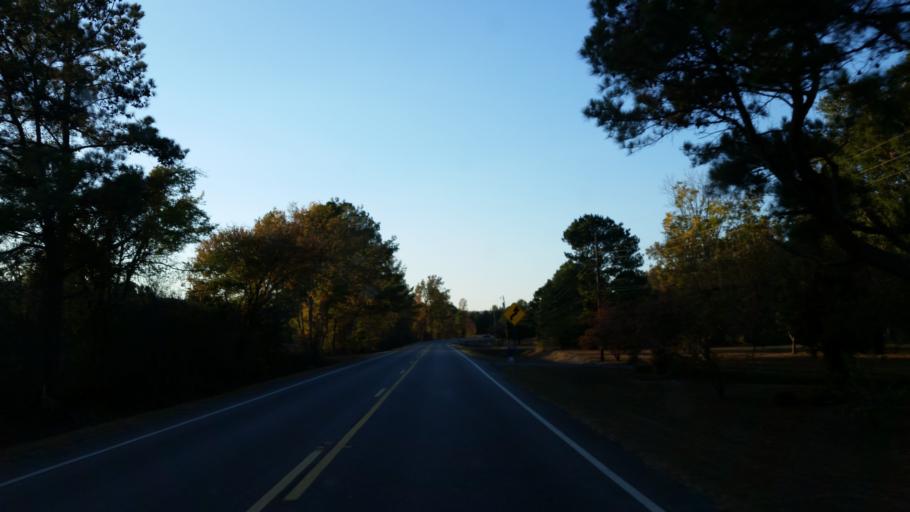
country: US
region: Georgia
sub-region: Gordon County
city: Calhoun
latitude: 34.5428
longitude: -84.9996
